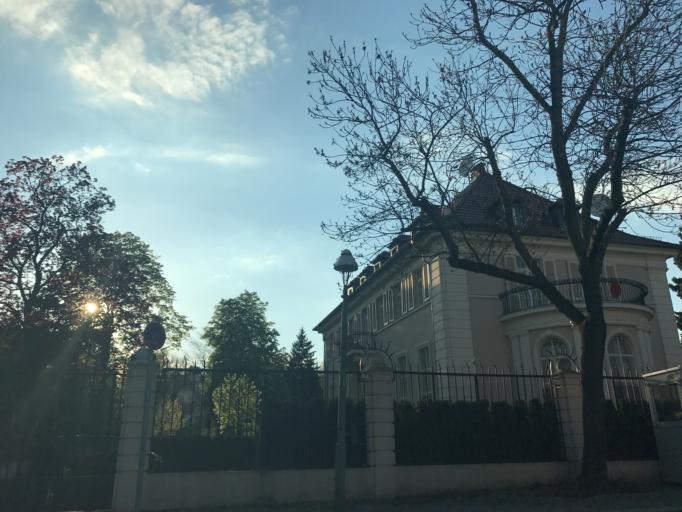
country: DE
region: Berlin
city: Westend
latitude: 52.5153
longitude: 13.2650
